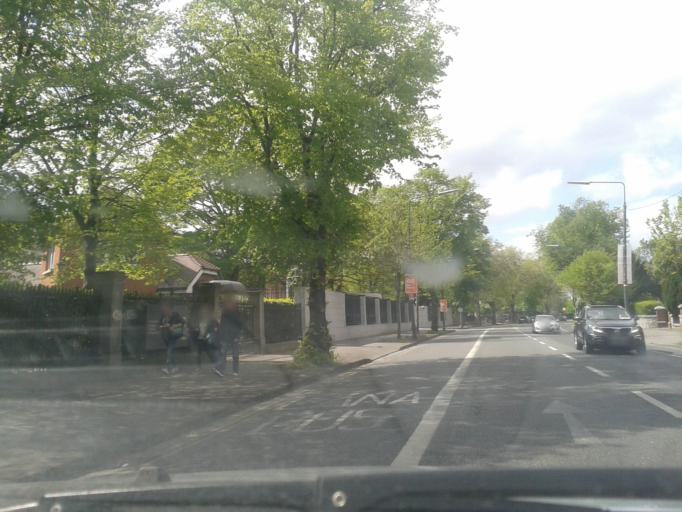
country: IE
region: Leinster
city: Donnybrook
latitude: 53.3249
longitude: -6.2222
